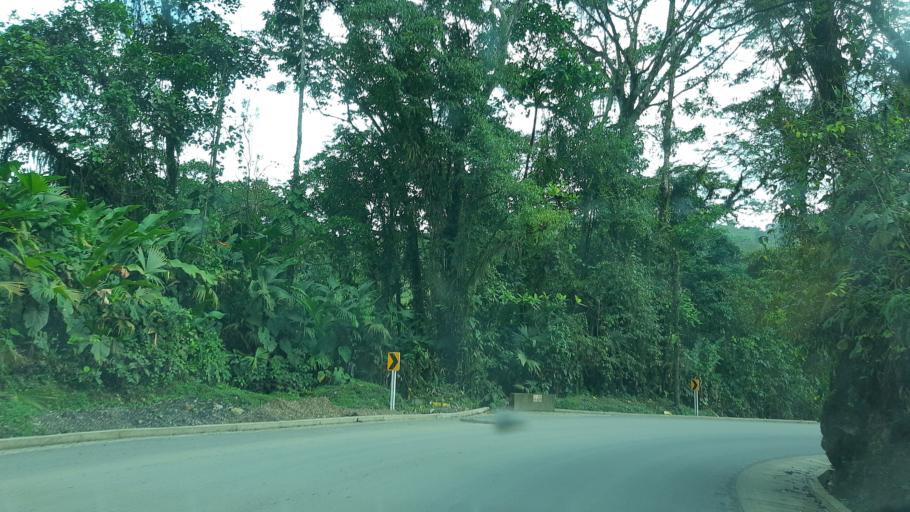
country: CO
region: Boyaca
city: Santa Maria
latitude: 4.8762
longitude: -73.2446
